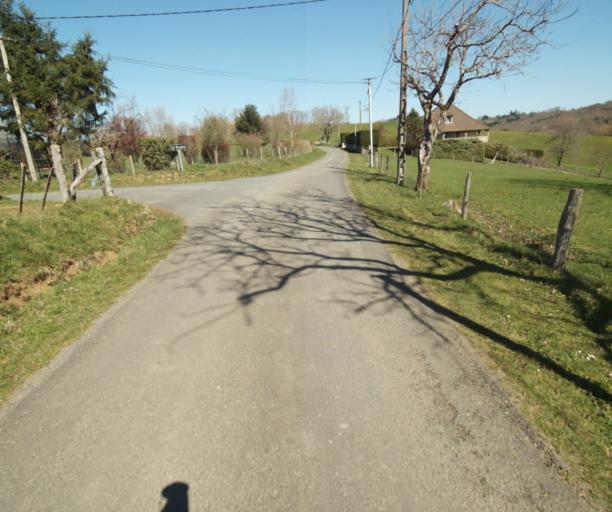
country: FR
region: Limousin
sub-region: Departement de la Correze
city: Saint-Clement
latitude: 45.3206
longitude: 1.7098
